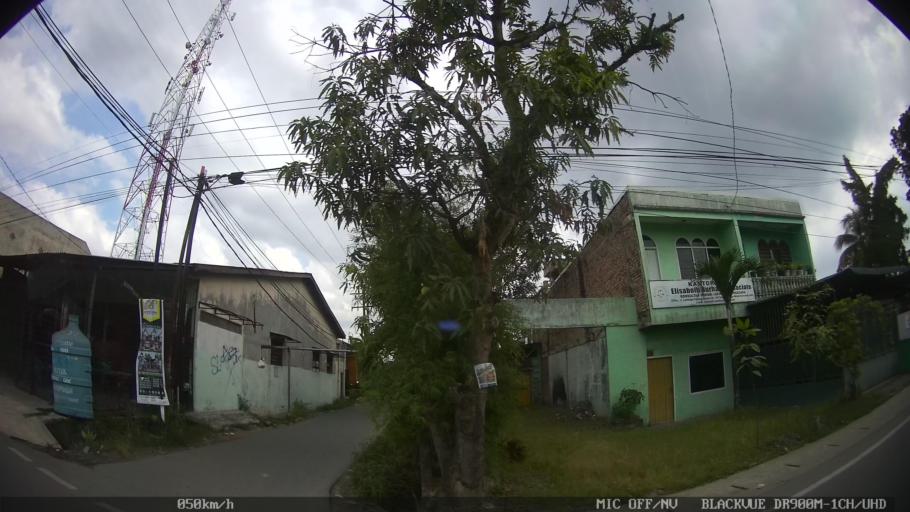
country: ID
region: North Sumatra
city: Sunggal
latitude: 3.6186
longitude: 98.6076
